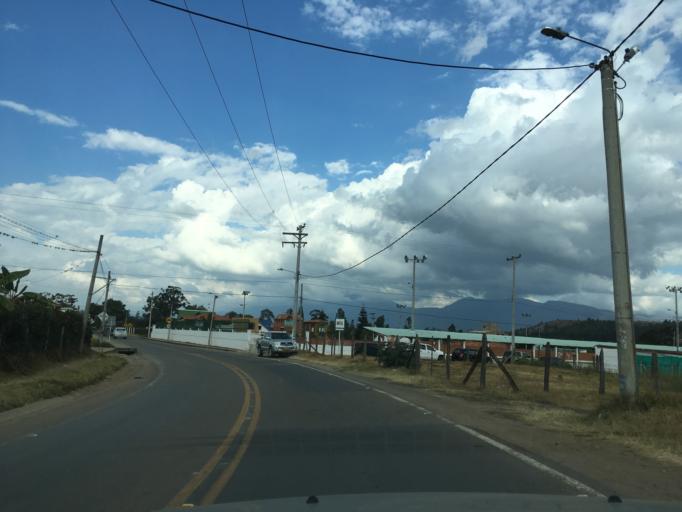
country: CO
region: Boyaca
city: Sutamarchan
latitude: 5.6169
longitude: -73.6216
